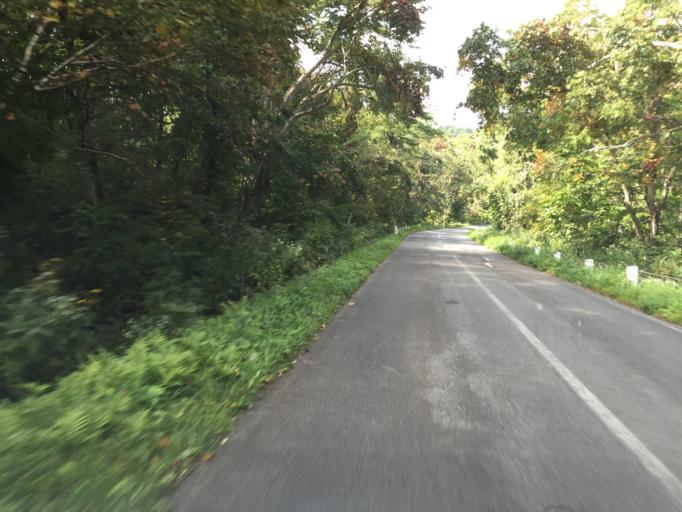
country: JP
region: Fukushima
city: Inawashiro
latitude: 37.6414
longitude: 140.0514
